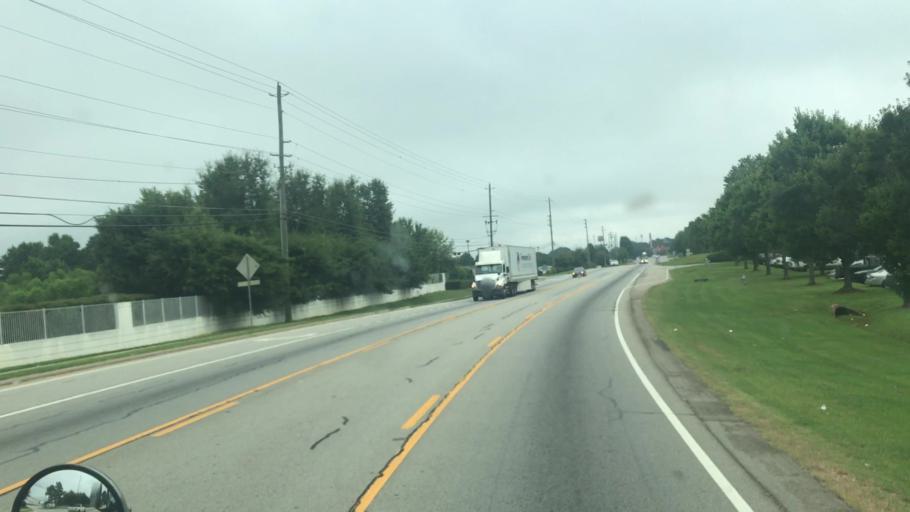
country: US
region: Georgia
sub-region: Henry County
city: McDonough
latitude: 33.4053
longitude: -84.1717
